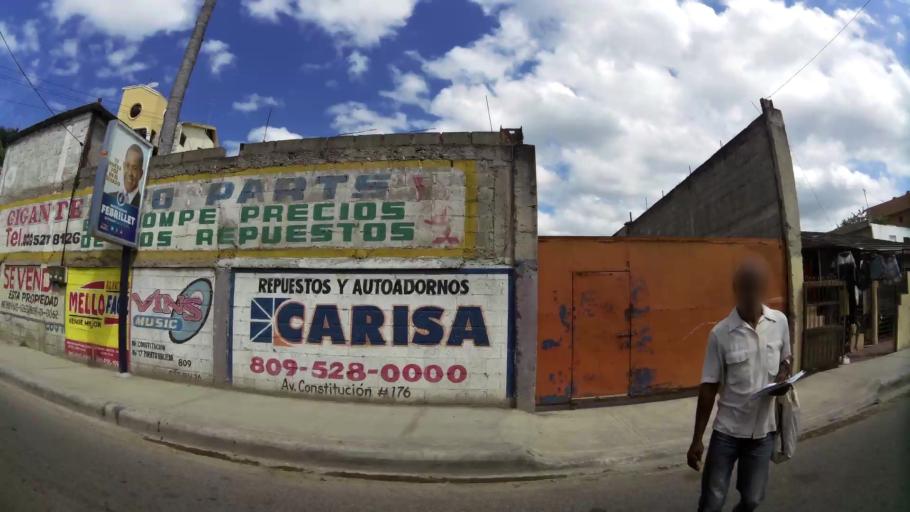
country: DO
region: San Cristobal
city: San Cristobal
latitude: 18.4291
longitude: -70.1239
